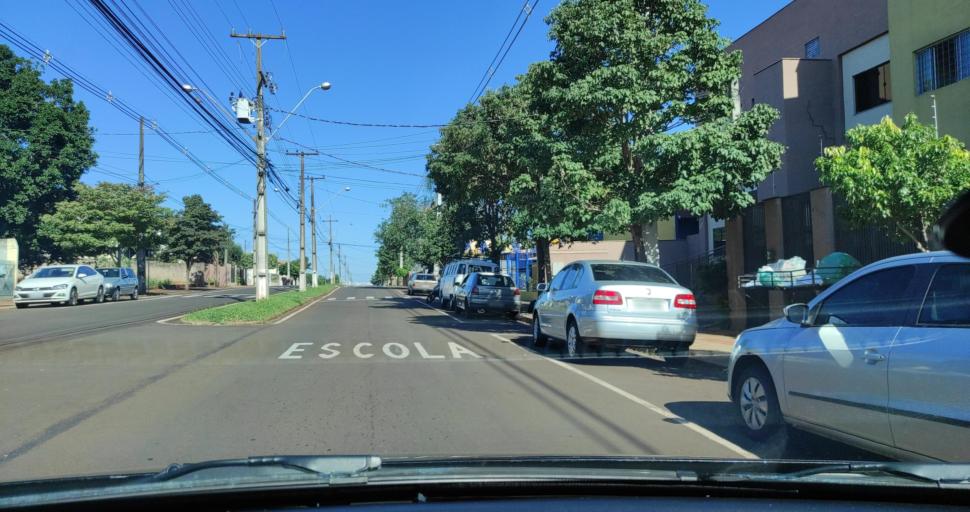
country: BR
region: Parana
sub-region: Ibipora
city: Ibipora
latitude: -23.2714
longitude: -51.0610
